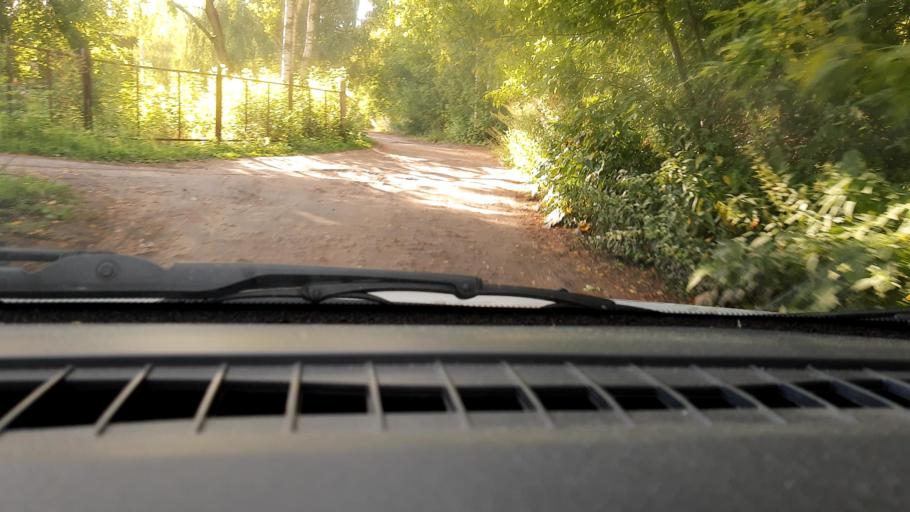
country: RU
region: Nizjnij Novgorod
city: Sitniki
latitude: 56.4520
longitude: 44.0182
